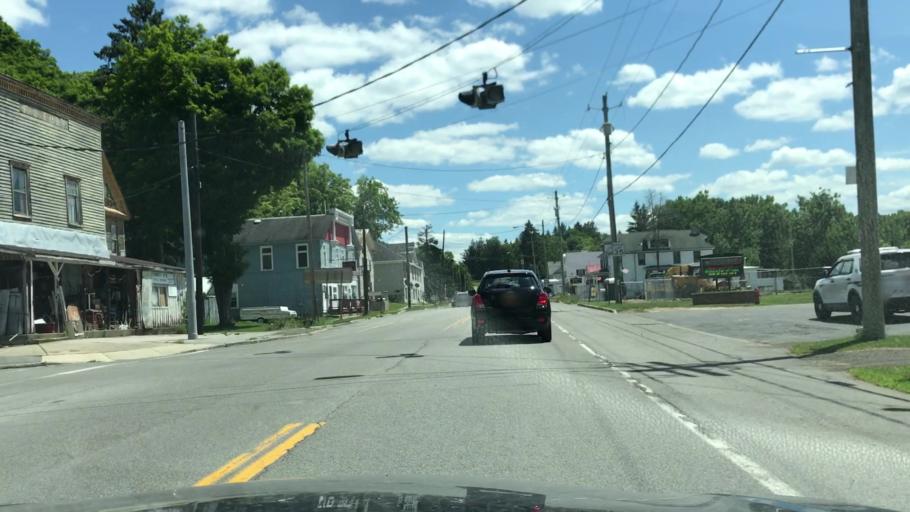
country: US
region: New York
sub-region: Wyoming County
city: Attica
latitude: 42.7622
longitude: -78.3135
